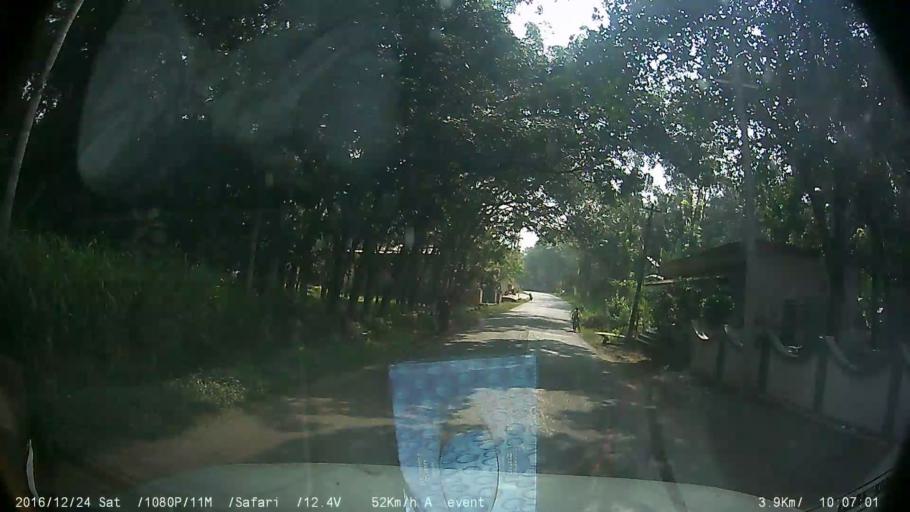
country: IN
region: Kerala
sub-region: Kottayam
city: Palackattumala
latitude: 9.7822
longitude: 76.5892
